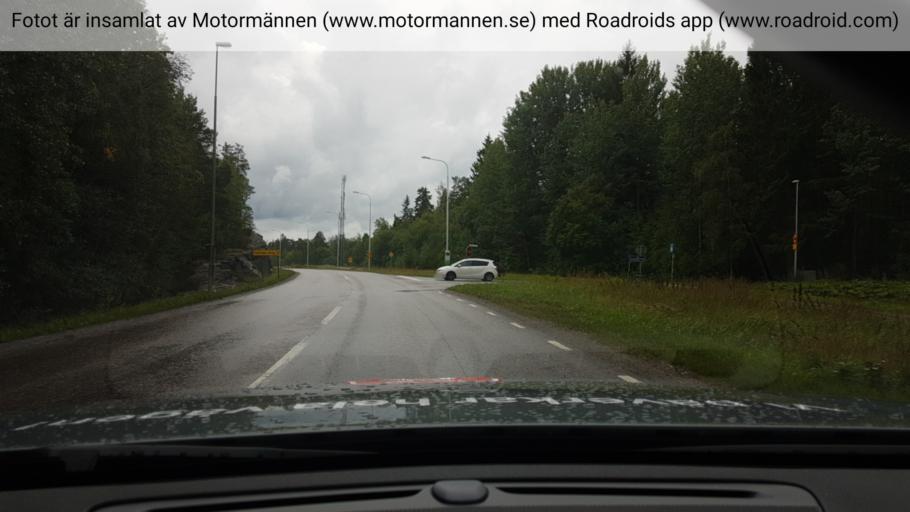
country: SE
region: Stockholm
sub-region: Botkyrka Kommun
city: Tullinge
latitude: 59.2027
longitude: 17.9251
